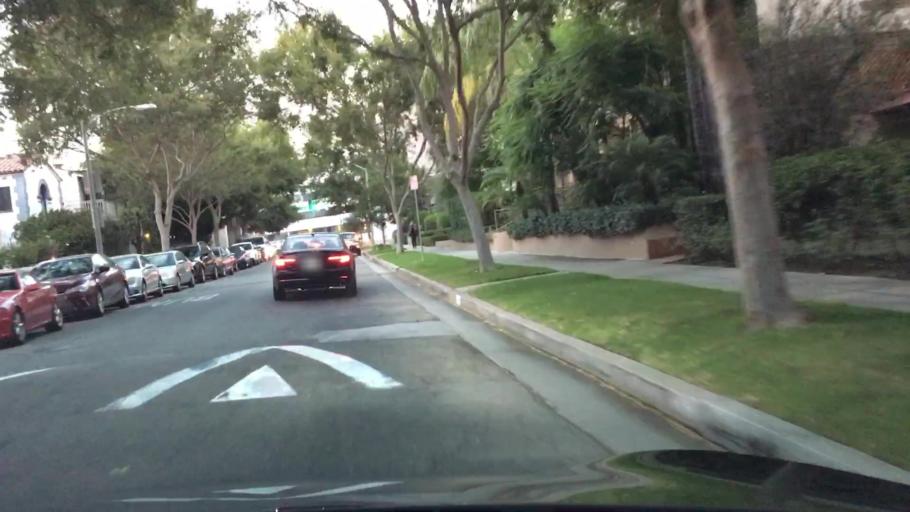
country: US
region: California
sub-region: Los Angeles County
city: Beverly Hills
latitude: 34.0656
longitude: -118.3959
